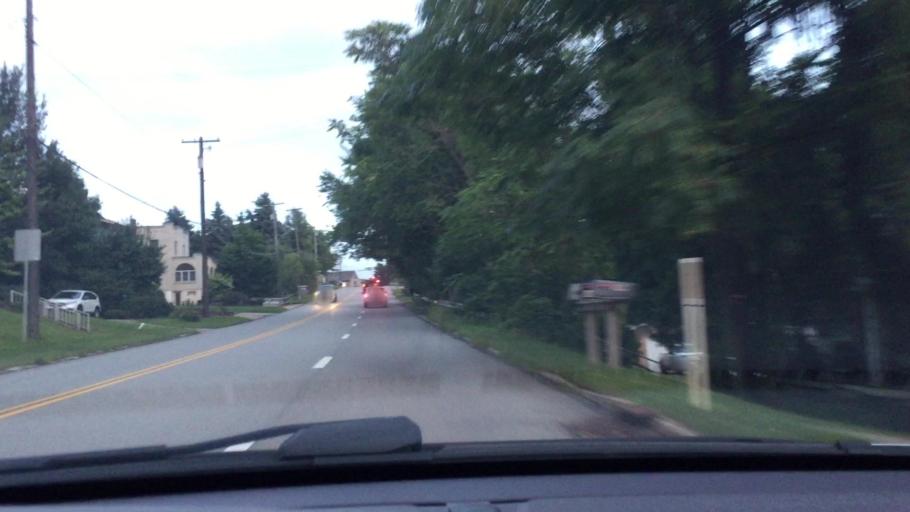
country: US
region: Pennsylvania
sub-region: Washington County
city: East Washington
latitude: 40.1564
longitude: -80.2159
